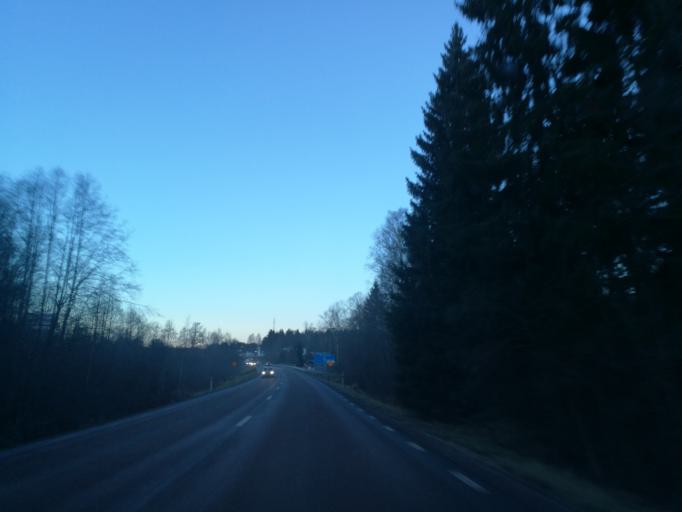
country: SE
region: Vaermland
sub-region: Eda Kommun
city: Charlottenberg
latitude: 59.9168
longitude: 12.2738
